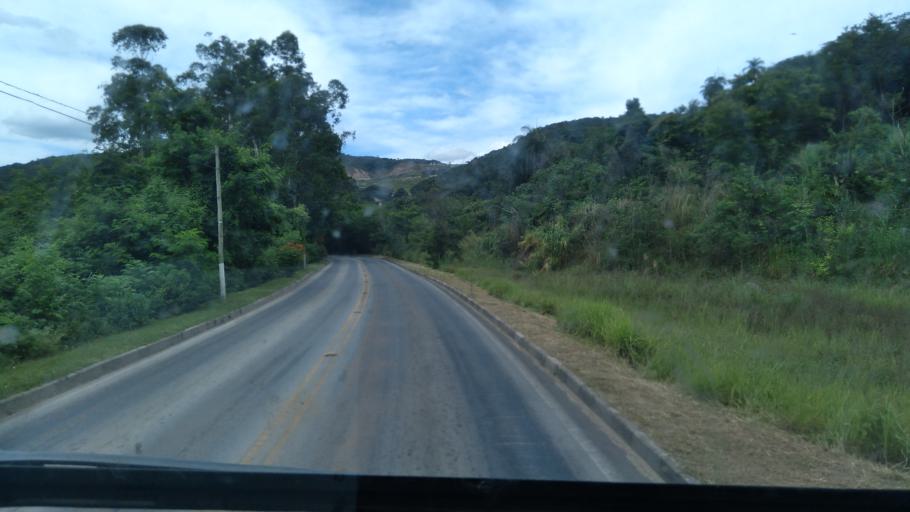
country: BR
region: Minas Gerais
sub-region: Santa Luzia
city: Santa Luzia
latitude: -19.8667
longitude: -43.8533
